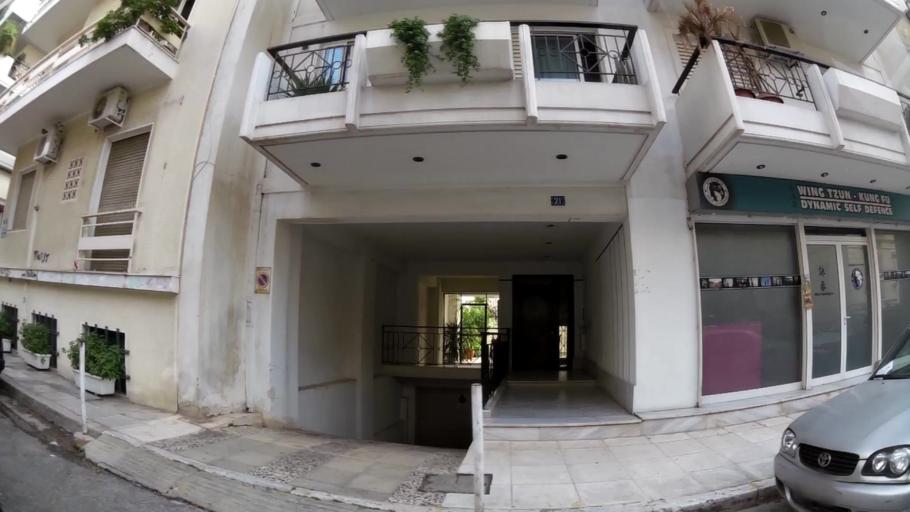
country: GR
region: Attica
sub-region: Nomarchia Athinas
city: Athens
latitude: 37.9656
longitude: 23.7237
